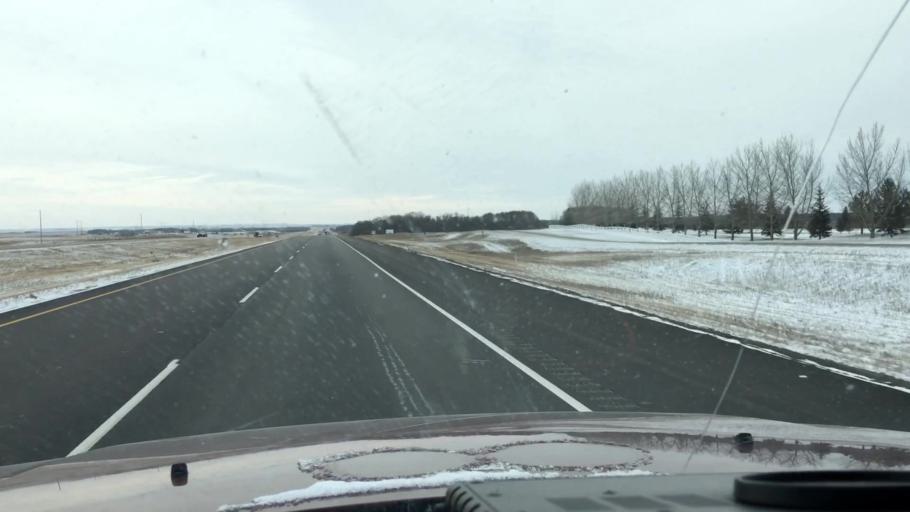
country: CA
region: Saskatchewan
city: Saskatoon
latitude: 51.9059
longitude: -106.5242
